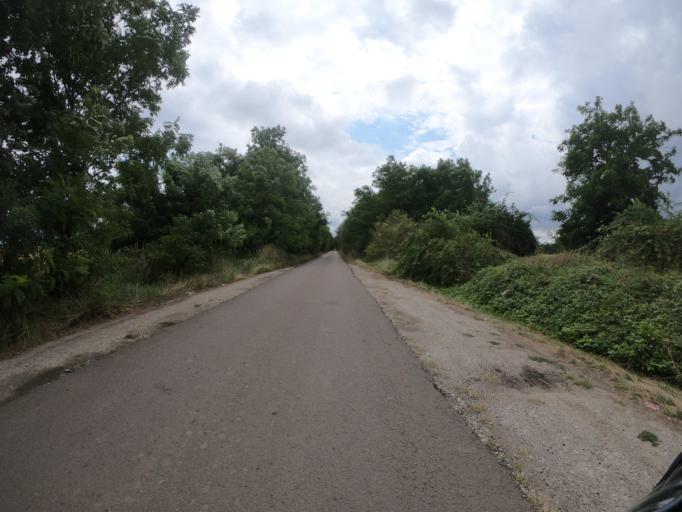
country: HU
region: Borsod-Abauj-Zemplen
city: Szentistvan
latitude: 47.7310
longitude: 20.6842
